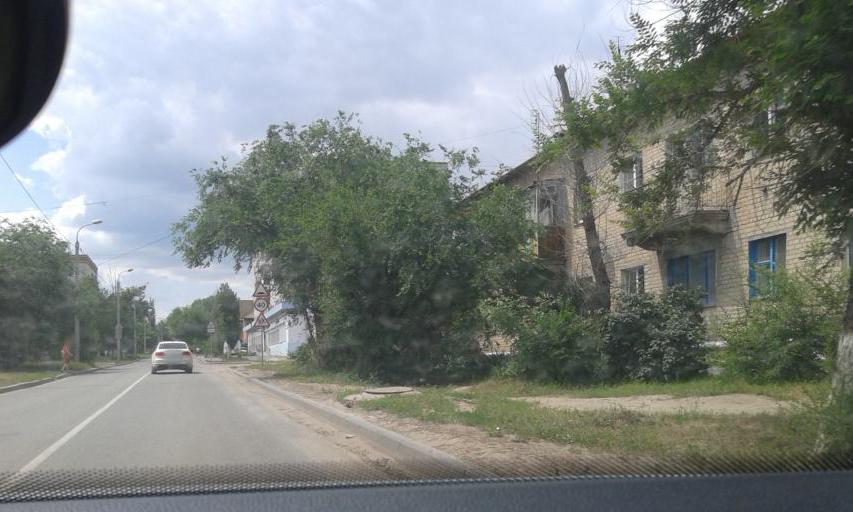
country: RU
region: Volgograd
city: Gorodishche
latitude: 48.7723
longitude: 44.4850
